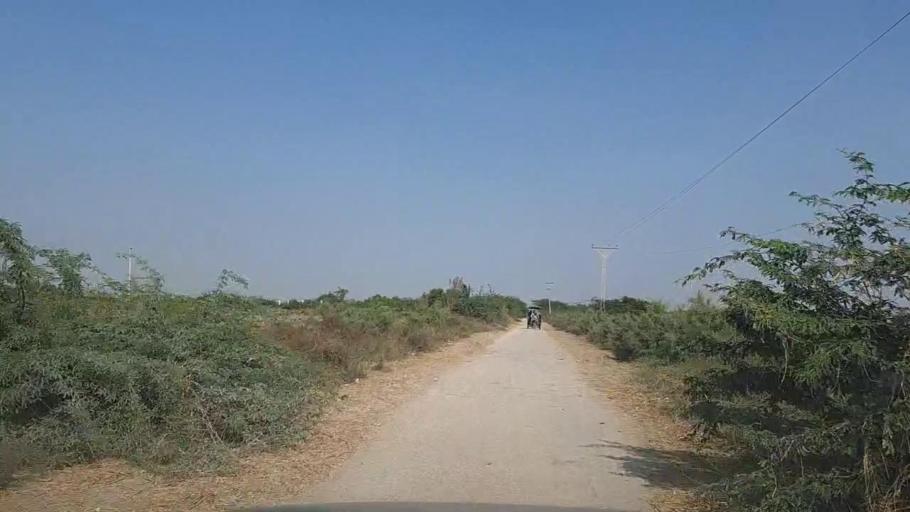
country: PK
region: Sindh
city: Thatta
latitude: 24.6014
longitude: 67.9527
